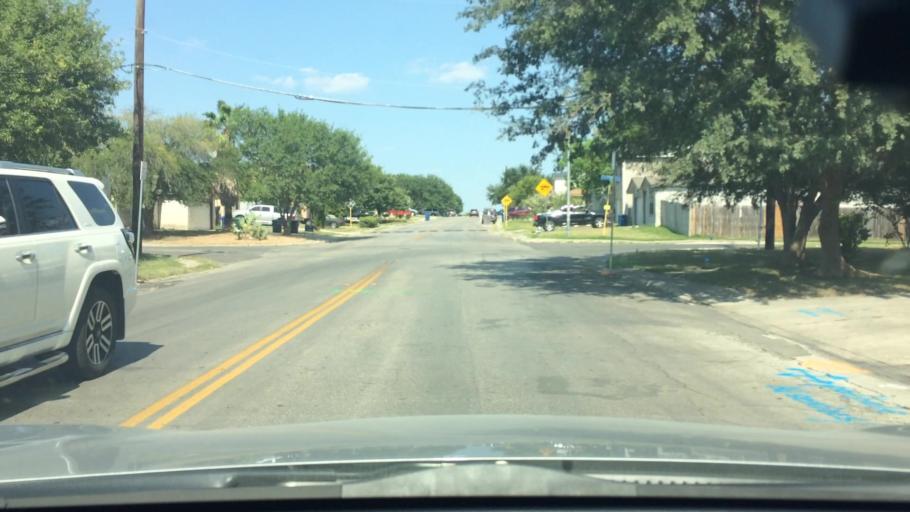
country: US
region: Texas
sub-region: Bexar County
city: Kirby
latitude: 29.4685
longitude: -98.3692
